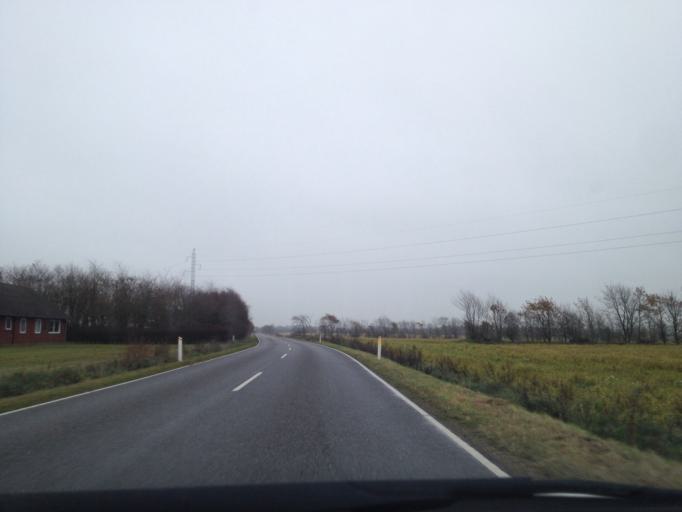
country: DK
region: South Denmark
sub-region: Tonder Kommune
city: Sherrebek
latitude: 55.0658
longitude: 8.7417
